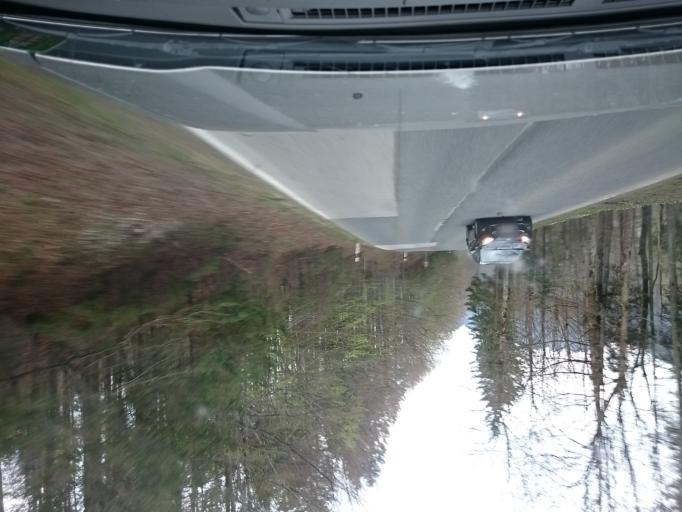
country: DE
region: Bavaria
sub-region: Upper Bavaria
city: Ettal
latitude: 47.5691
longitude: 11.0718
